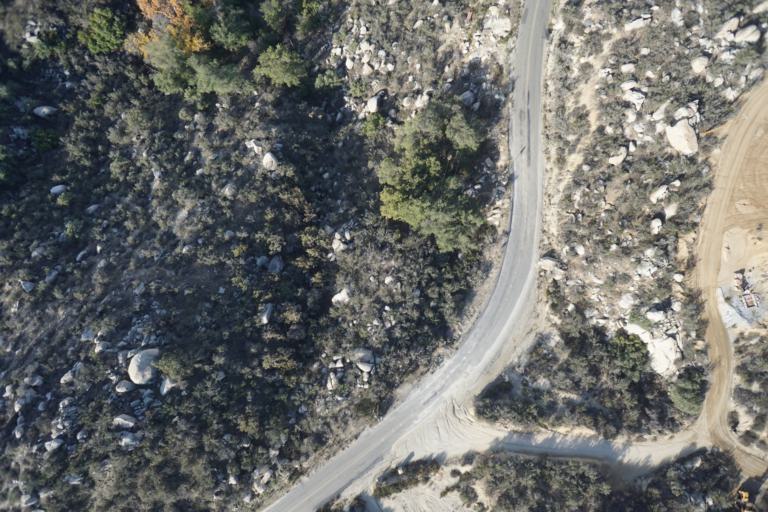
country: US
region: California
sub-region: Riverside County
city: East Hemet
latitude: 33.6421
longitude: -116.9247
